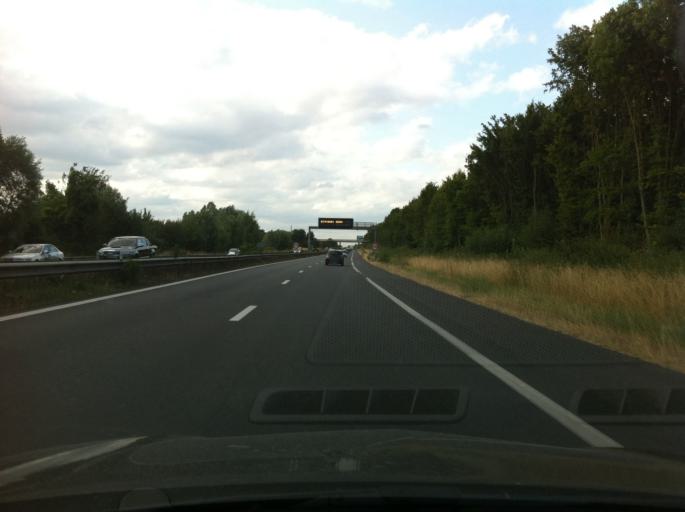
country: FR
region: Ile-de-France
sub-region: Departement de Seine-et-Marne
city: Brie-Comte-Robert
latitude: 48.6897
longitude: 2.5958
